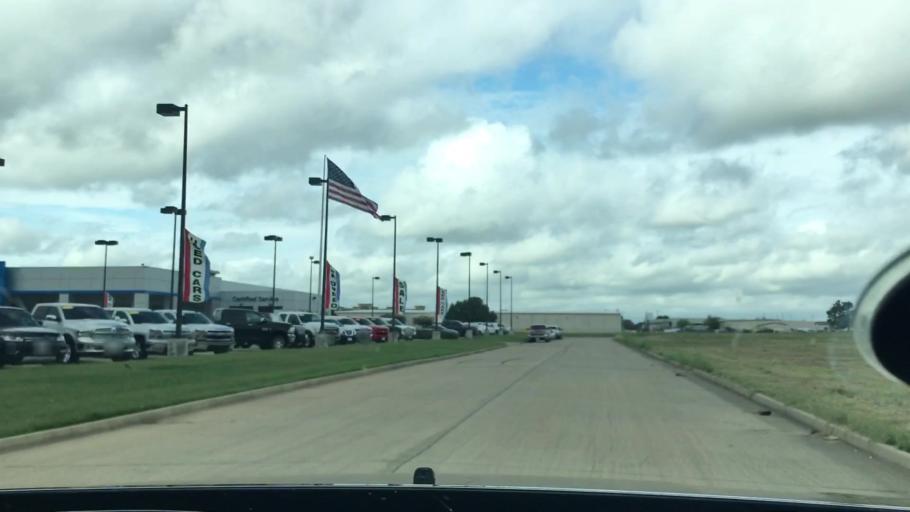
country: US
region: Oklahoma
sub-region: Bryan County
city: Durant
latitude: 34.0029
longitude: -96.4030
